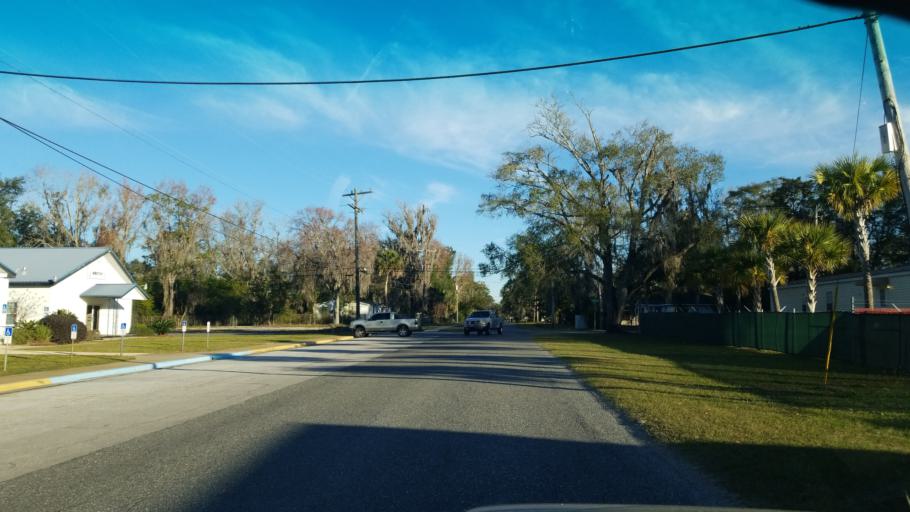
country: US
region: Florida
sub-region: Duval County
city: Baldwin
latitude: 30.3157
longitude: -81.8444
